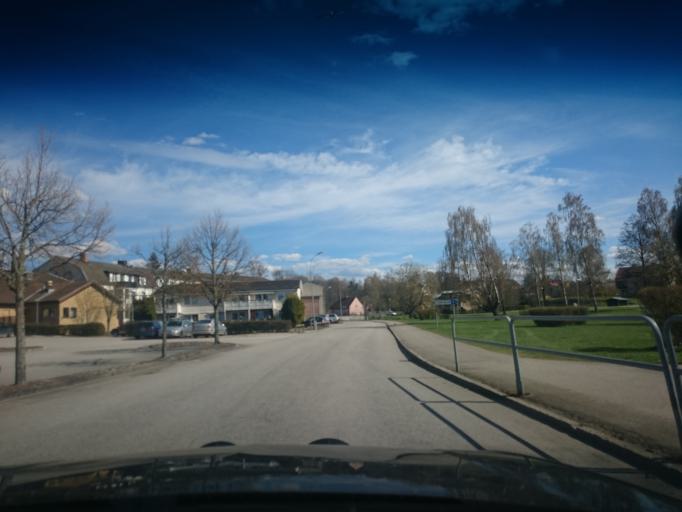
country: SE
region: Kalmar
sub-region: Hultsfreds Kommun
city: Virserum
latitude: 57.3185
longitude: 15.5813
